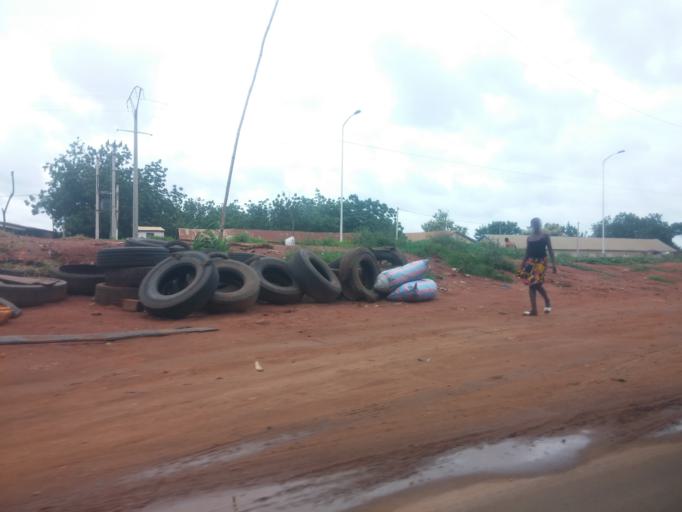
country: TG
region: Maritime
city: Tsevie
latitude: 6.3206
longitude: 1.2178
